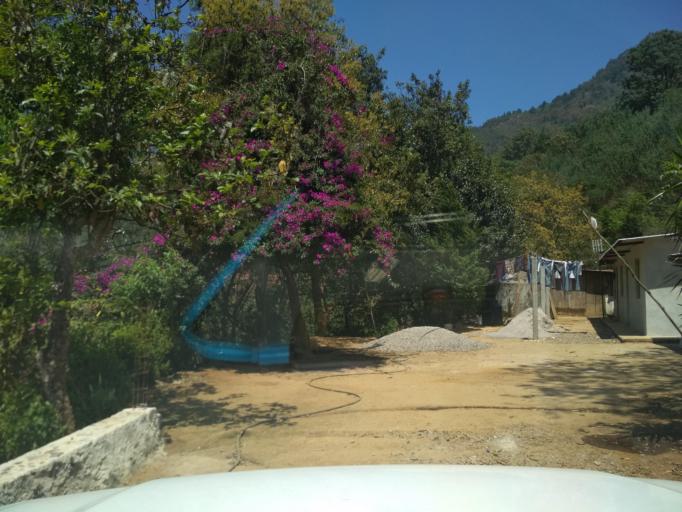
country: MX
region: Veracruz
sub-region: Tlilapan
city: Tonalixco
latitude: 18.7800
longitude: -97.0762
